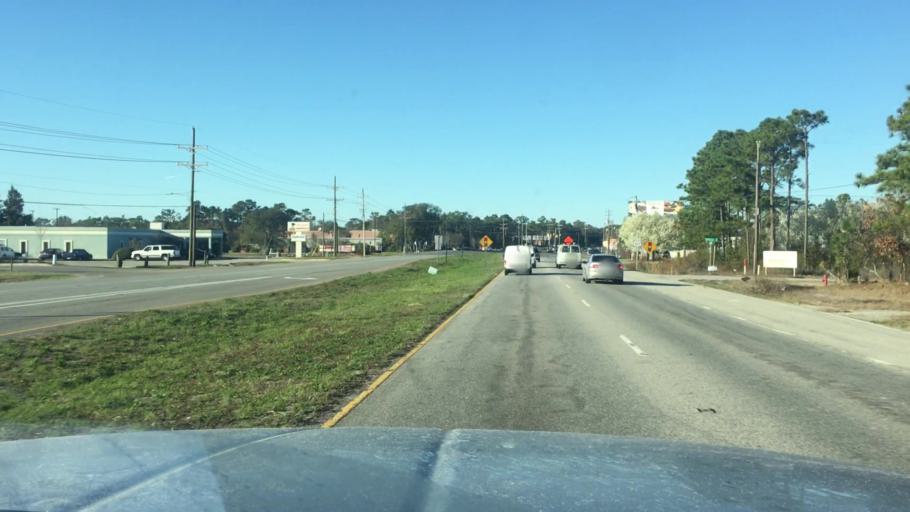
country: US
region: North Carolina
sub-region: New Hanover County
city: Myrtle Grove
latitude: 34.1225
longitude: -77.8999
